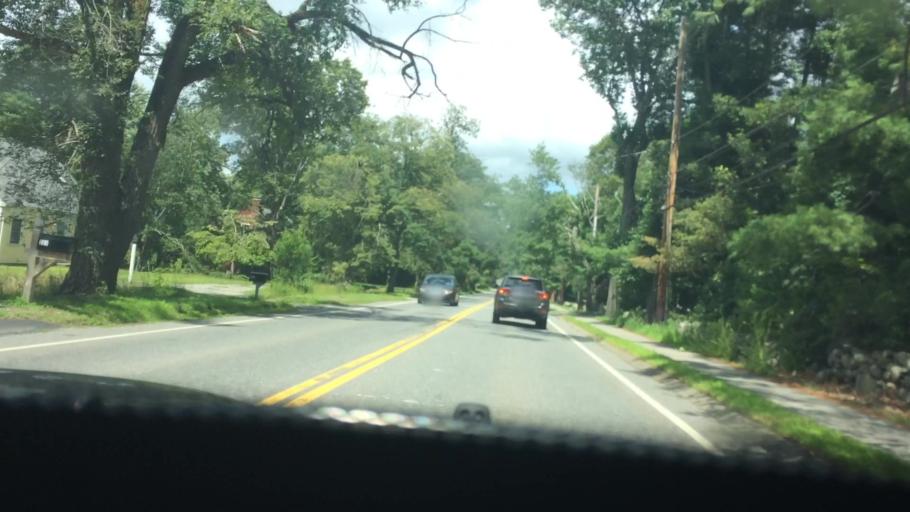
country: US
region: Massachusetts
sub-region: Middlesex County
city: Sudbury
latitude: 42.3968
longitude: -71.4296
